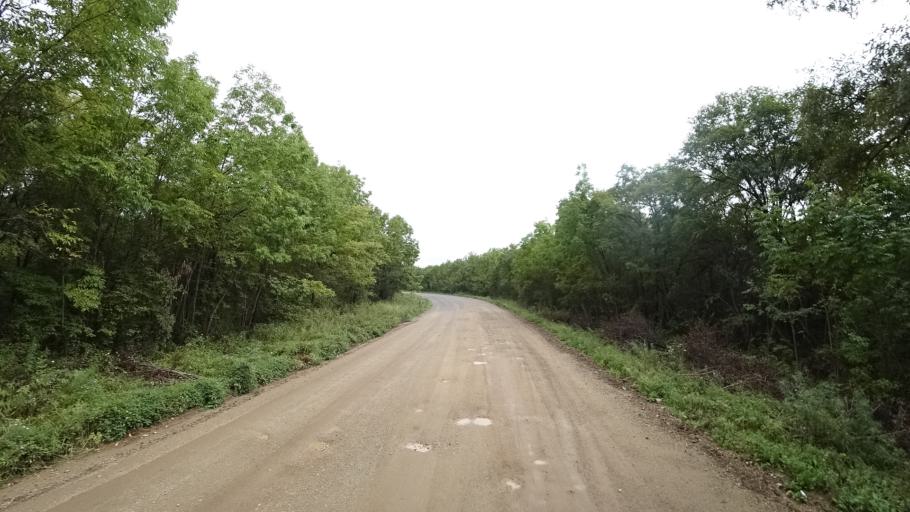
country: RU
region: Primorskiy
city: Lyalichi
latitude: 44.0772
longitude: 132.4557
